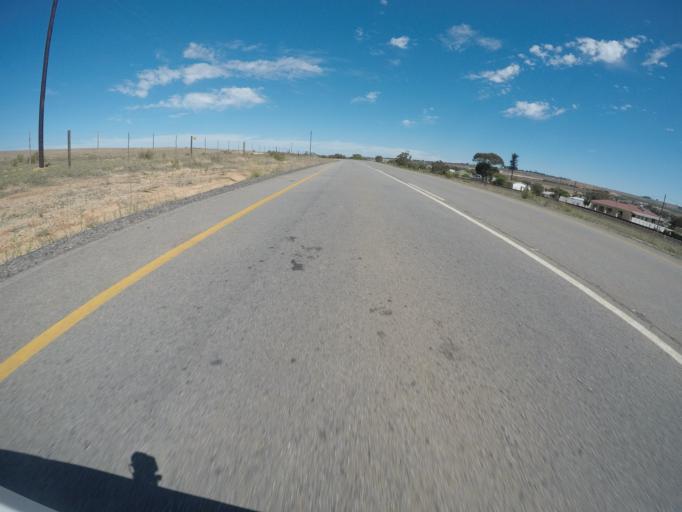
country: ZA
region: Western Cape
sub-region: West Coast District Municipality
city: Malmesbury
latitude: -33.4869
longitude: 18.6883
